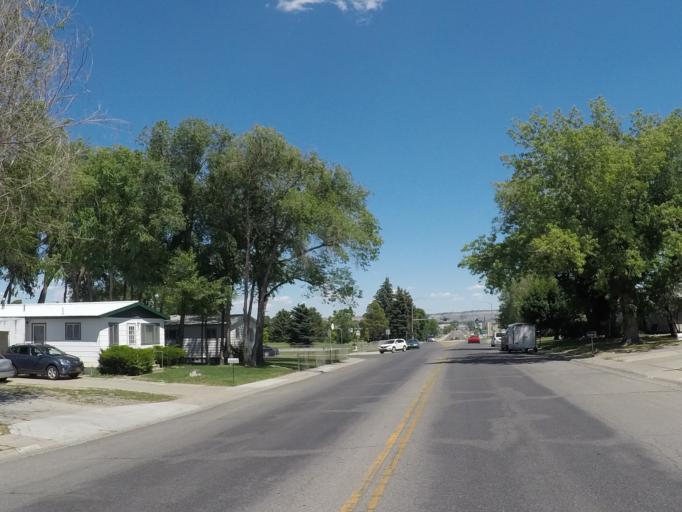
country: US
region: Montana
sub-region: Yellowstone County
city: Billings
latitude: 45.7625
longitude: -108.5688
